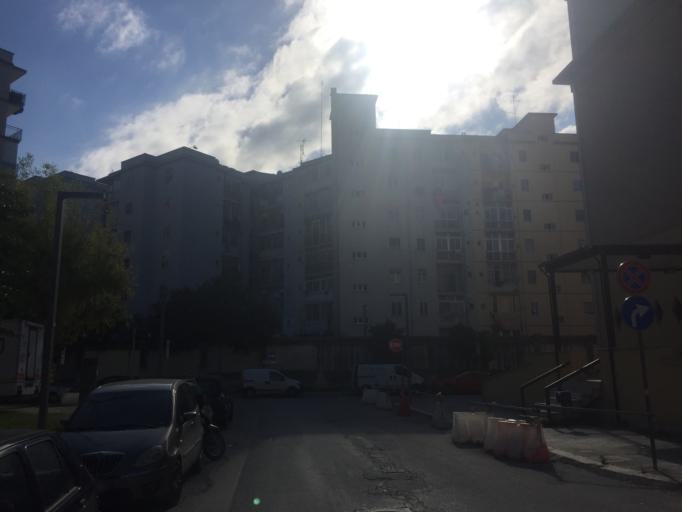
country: IT
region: Apulia
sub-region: Provincia di Bari
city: Bari
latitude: 41.1106
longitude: 16.8596
